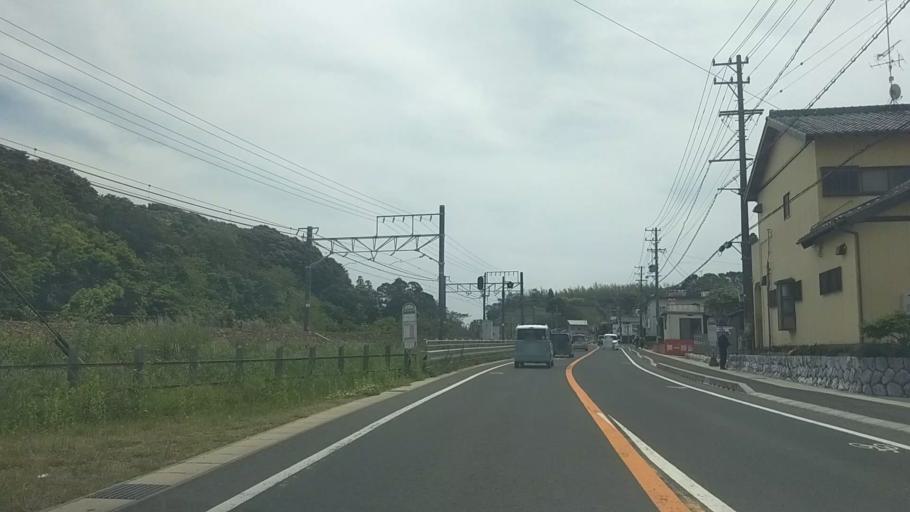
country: JP
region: Shizuoka
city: Kosai-shi
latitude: 34.7006
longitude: 137.5556
